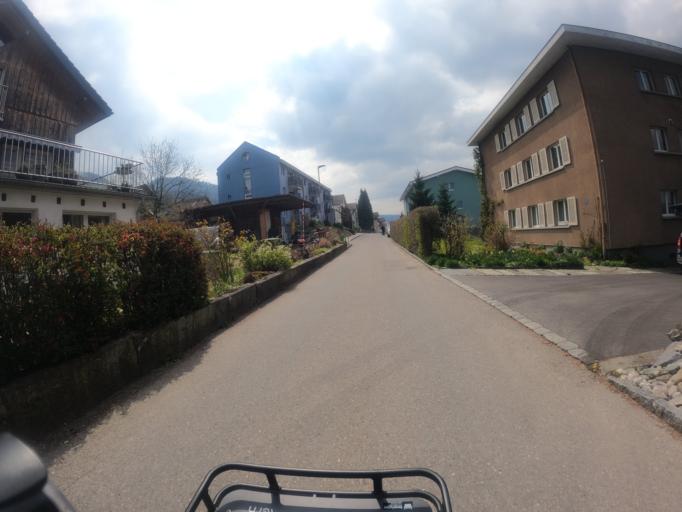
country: CH
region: Lucerne
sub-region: Lucerne-Land District
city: Root
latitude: 47.1196
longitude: 8.3960
